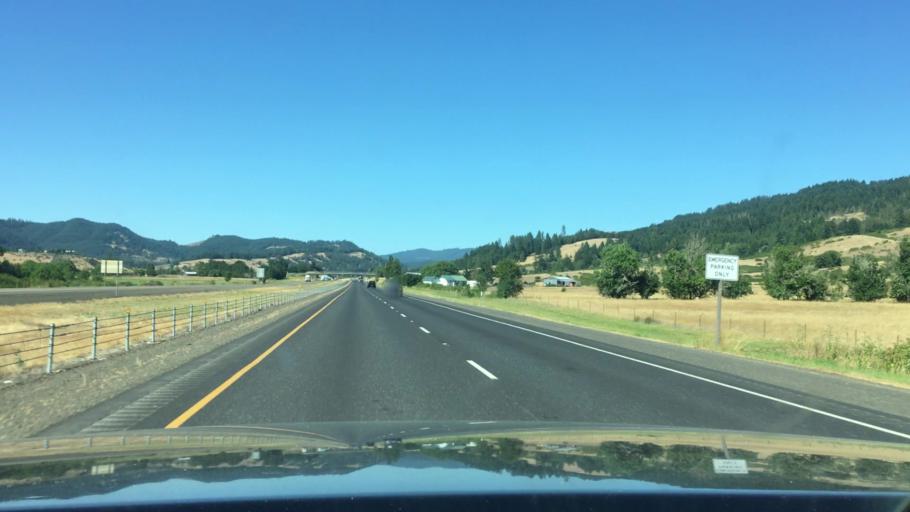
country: US
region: Oregon
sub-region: Douglas County
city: Yoncalla
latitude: 43.5733
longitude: -123.2688
